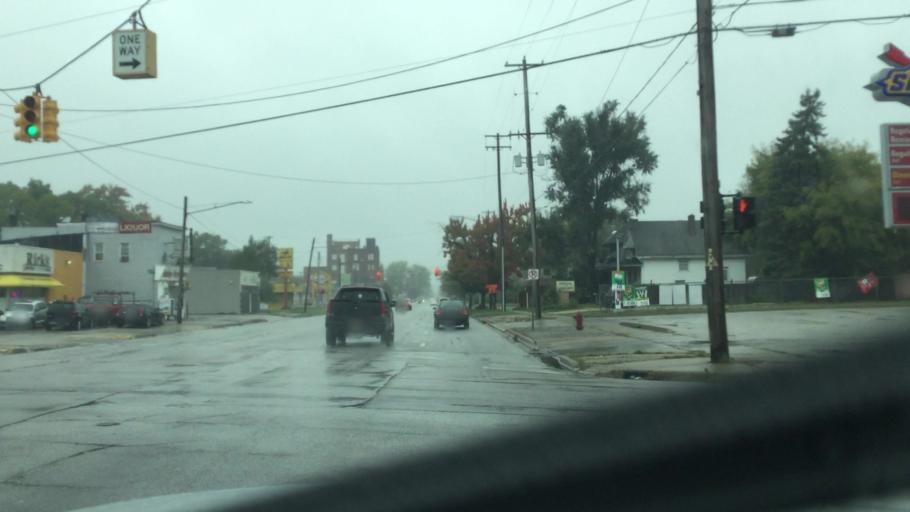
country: US
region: Michigan
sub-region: Saginaw County
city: Buena Vista
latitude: 43.4147
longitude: -83.9216
